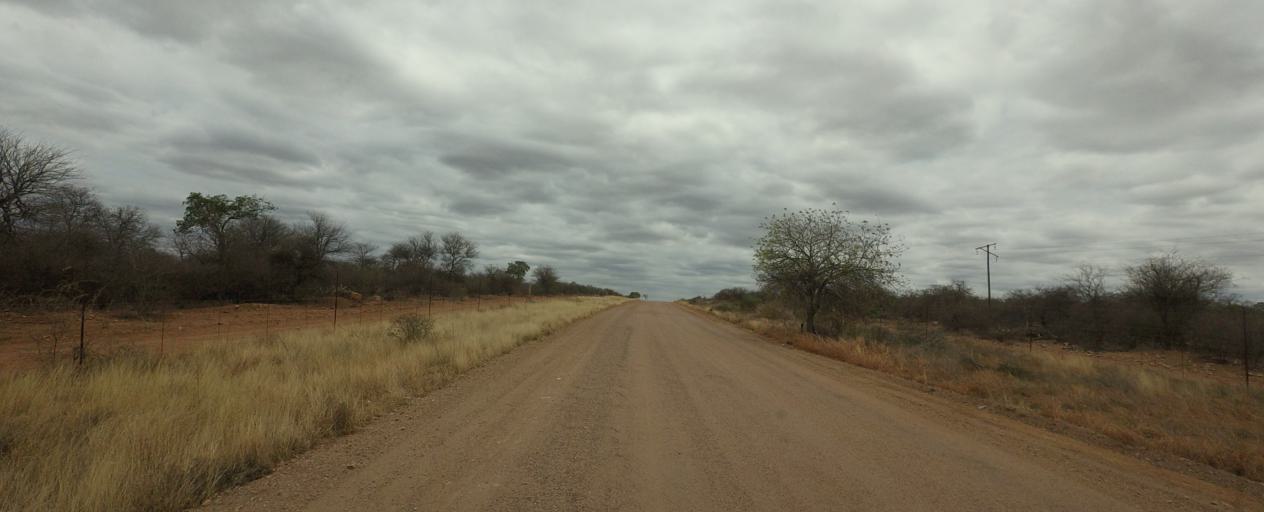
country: BW
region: Central
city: Mathathane
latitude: -22.7037
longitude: 28.6085
